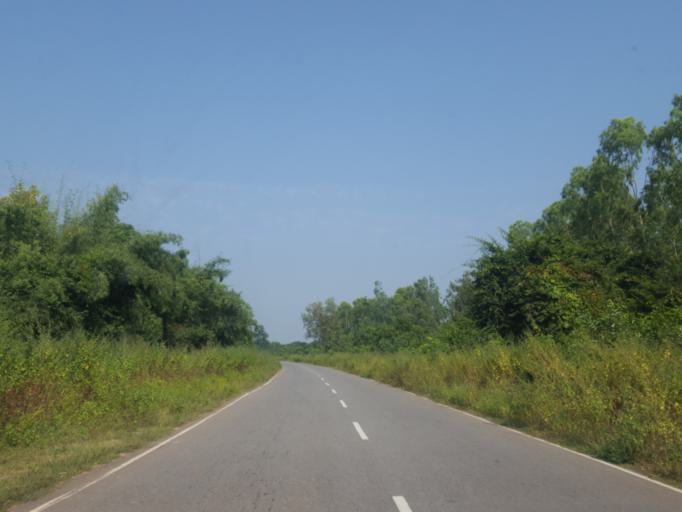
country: IN
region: Telangana
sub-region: Khammam
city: Yellandu
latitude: 17.6287
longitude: 80.3029
